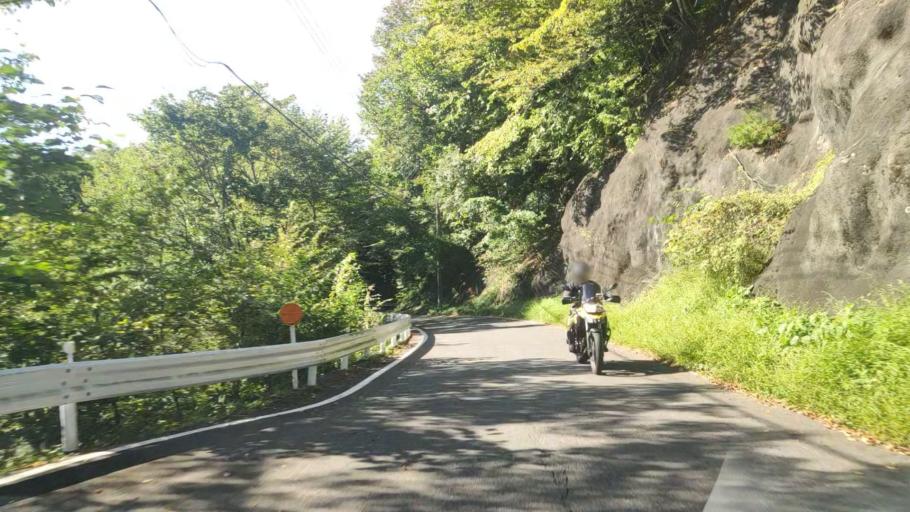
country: JP
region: Gunma
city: Nakanojomachi
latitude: 36.5991
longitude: 138.6848
